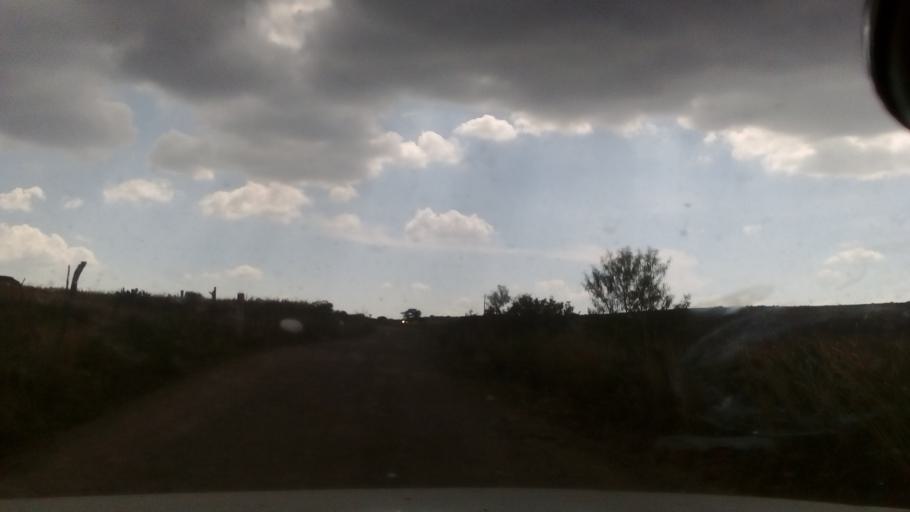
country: MX
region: Guanajuato
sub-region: Silao de la Victoria
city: San Francisco (Banos de Agua Caliente)
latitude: 21.1784
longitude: -101.4159
